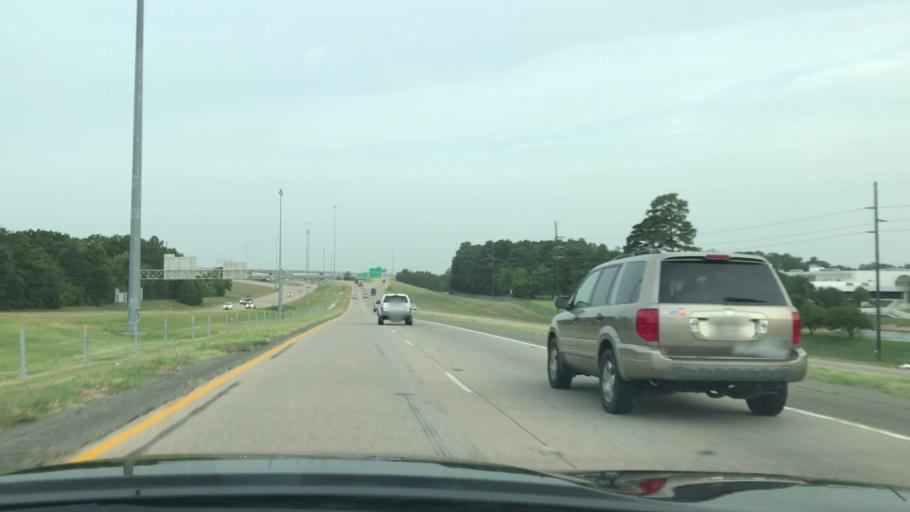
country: US
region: Louisiana
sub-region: Bossier Parish
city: Bossier City
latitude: 32.4164
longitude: -93.7385
